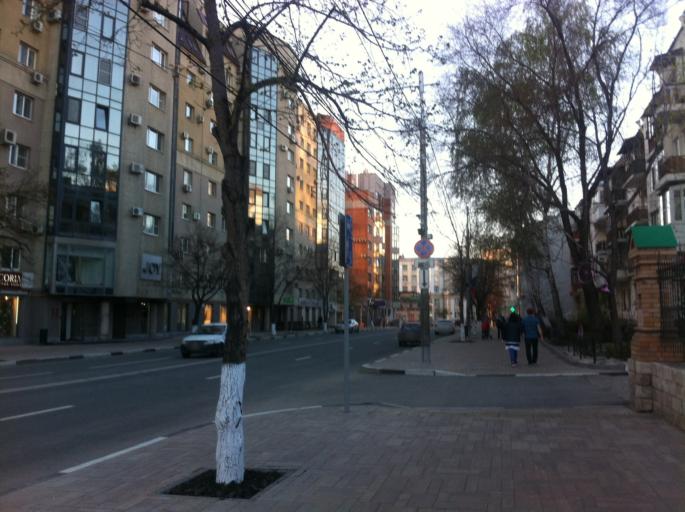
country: RU
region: Samara
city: Samara
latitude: 53.1981
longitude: 50.1040
